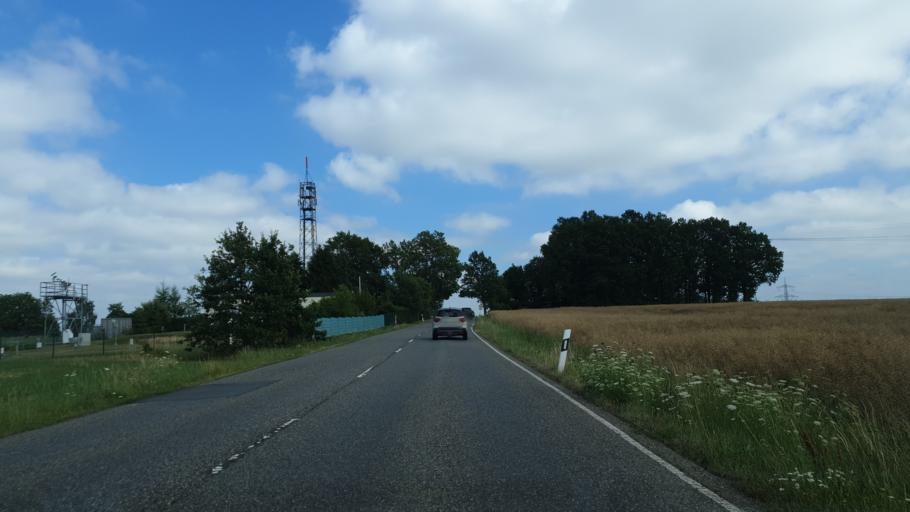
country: DE
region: Saxony
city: Neukirchen
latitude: 50.7915
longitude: 12.8712
